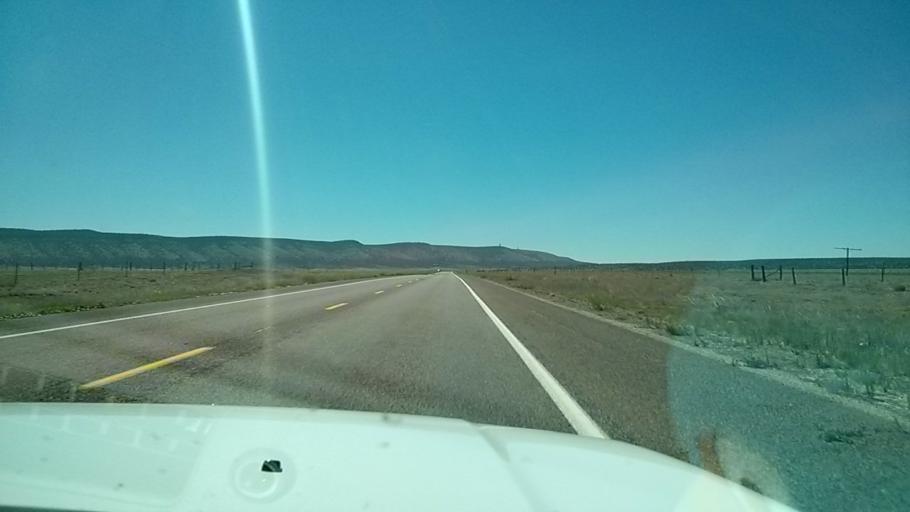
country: US
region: Arizona
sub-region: Mohave County
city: Peach Springs
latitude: 35.4015
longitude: -113.0174
